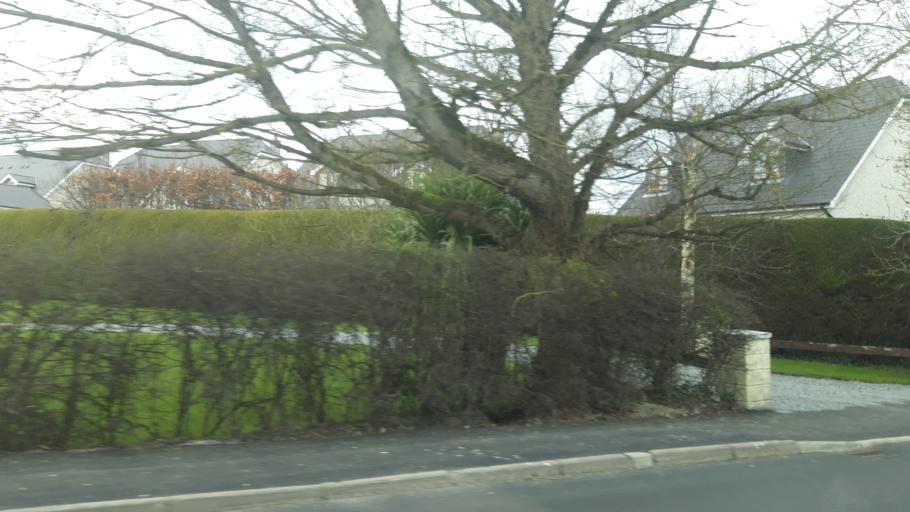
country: IE
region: Leinster
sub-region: Kildare
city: Clane
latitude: 53.2956
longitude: -6.6811
